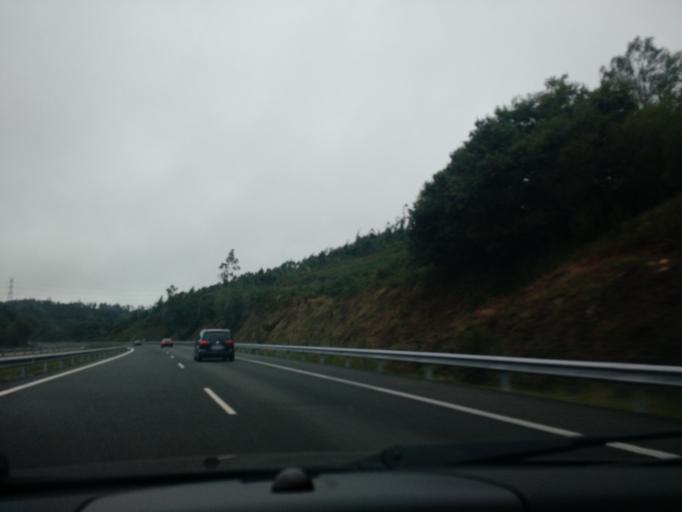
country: ES
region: Galicia
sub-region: Provincia da Coruna
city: Abegondo
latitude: 43.1690
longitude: -8.3206
